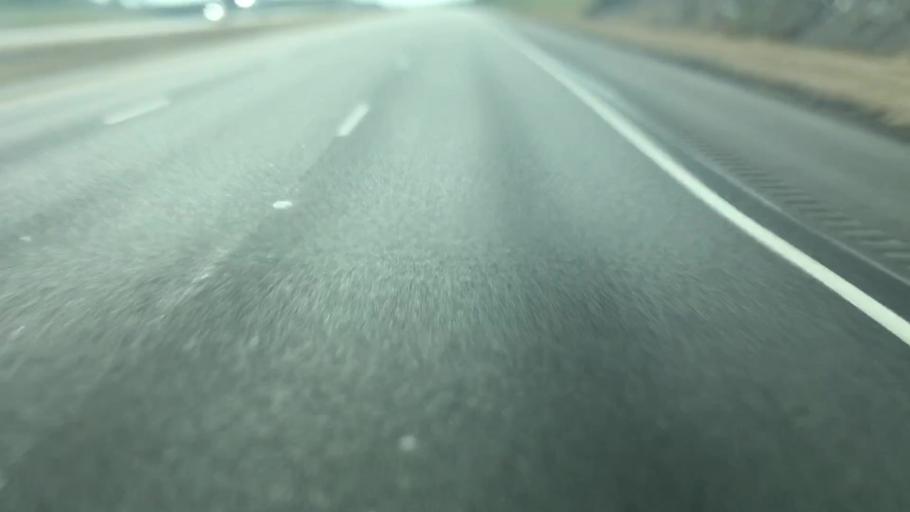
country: US
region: Alabama
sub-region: Walker County
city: Cordova
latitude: 33.7652
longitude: -87.2073
